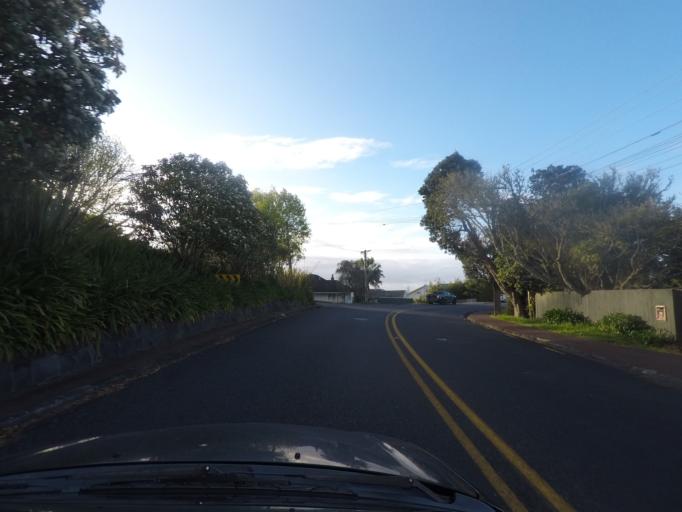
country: NZ
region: Auckland
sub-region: Auckland
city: Waitakere
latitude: -36.9201
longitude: 174.6579
